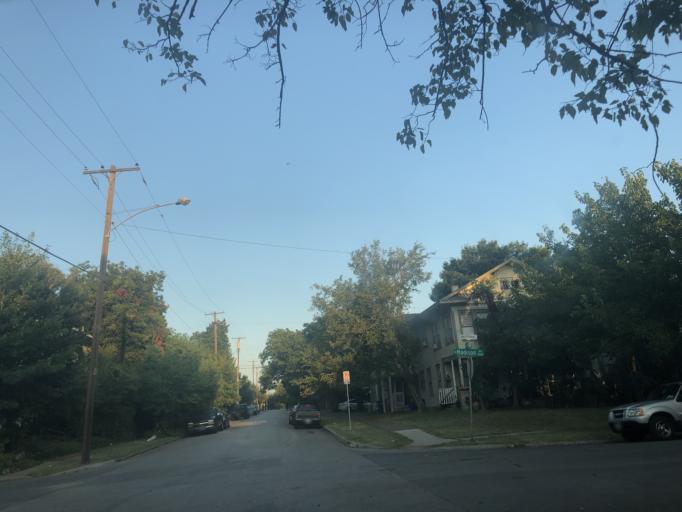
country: US
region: Texas
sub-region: Dallas County
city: Dallas
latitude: 32.7523
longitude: -96.8264
